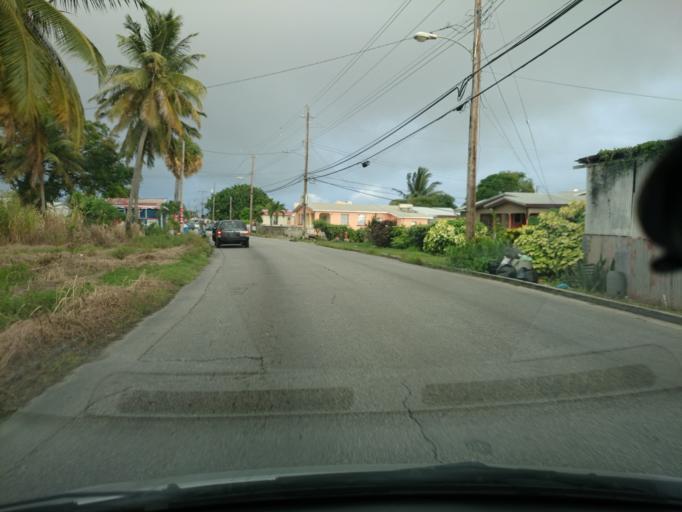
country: BB
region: Christ Church
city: Oistins
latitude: 13.0587
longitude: -59.5329
